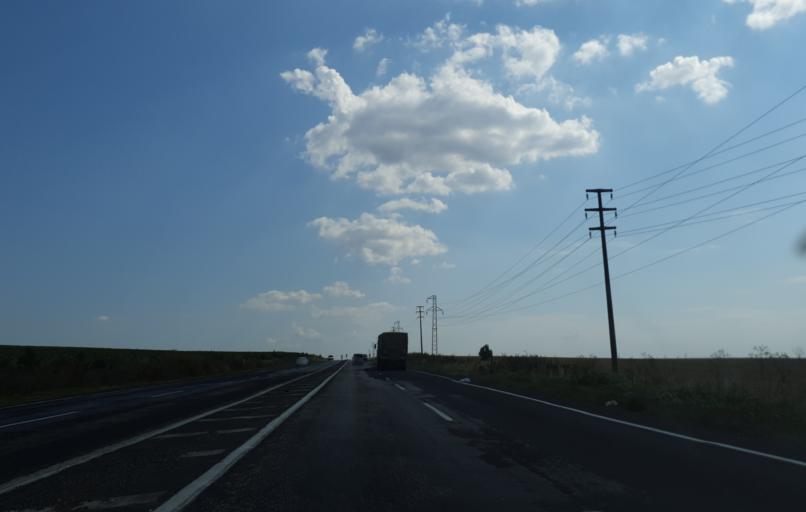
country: TR
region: Kirklareli
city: Buyukkaristiran
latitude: 41.2601
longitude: 27.5468
